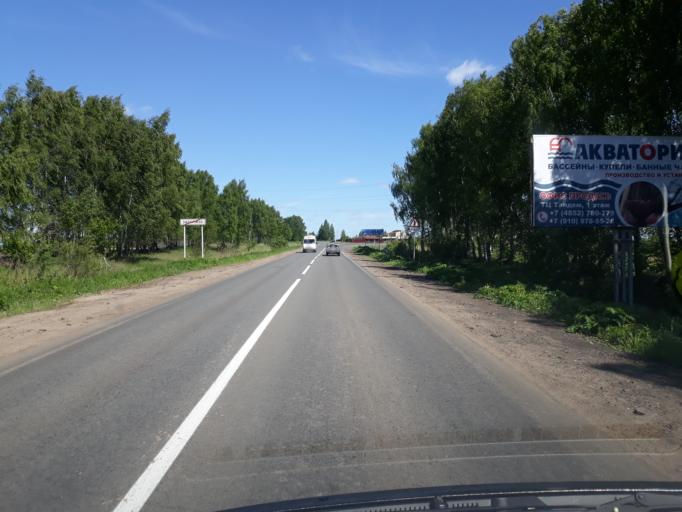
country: RU
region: Jaroslavl
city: Yaroslavl
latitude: 57.6692
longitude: 40.0204
